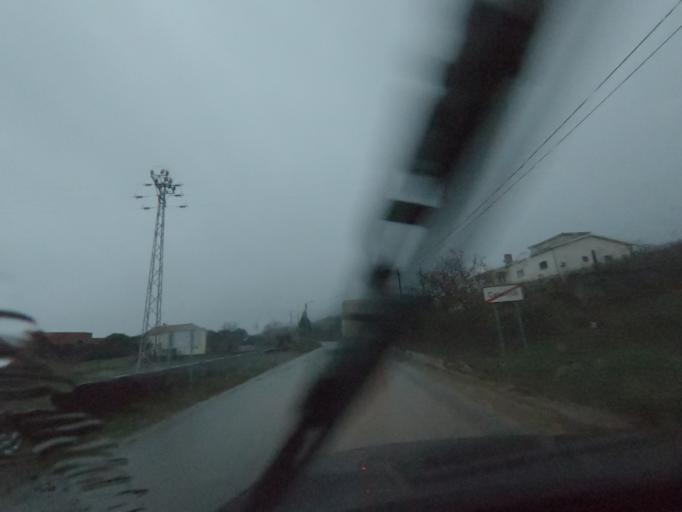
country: PT
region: Vila Real
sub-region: Sabrosa
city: Sabrosa
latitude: 41.2417
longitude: -7.5692
